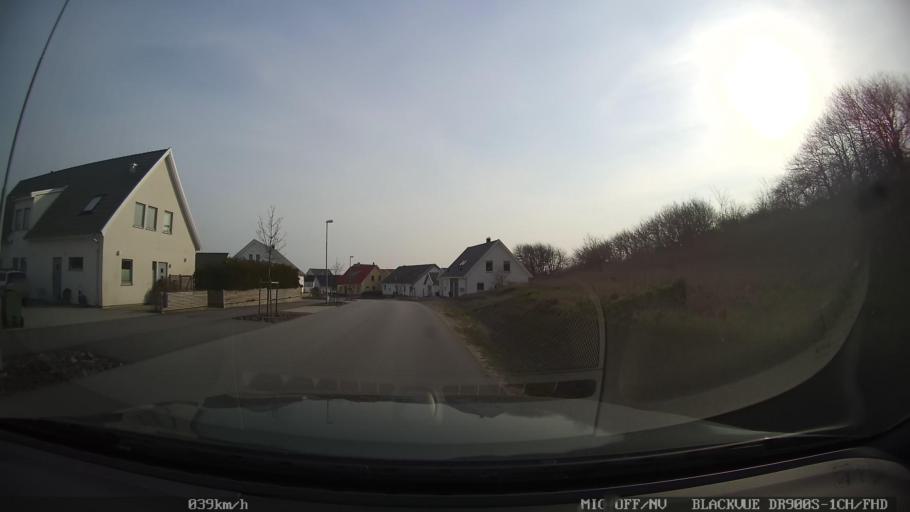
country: SE
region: Skane
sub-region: Ystads Kommun
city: Ystad
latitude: 55.4461
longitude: 13.7948
